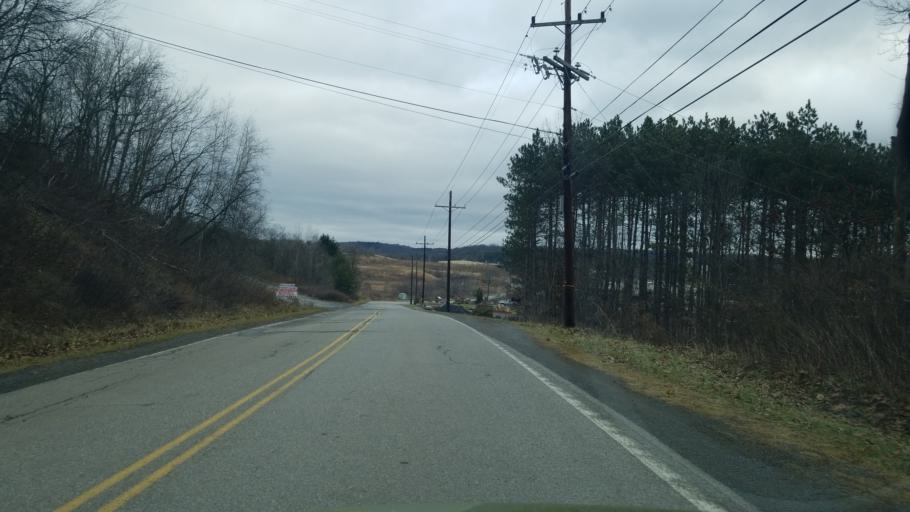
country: US
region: Pennsylvania
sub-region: Clearfield County
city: Clearfield
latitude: 41.0283
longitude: -78.4015
